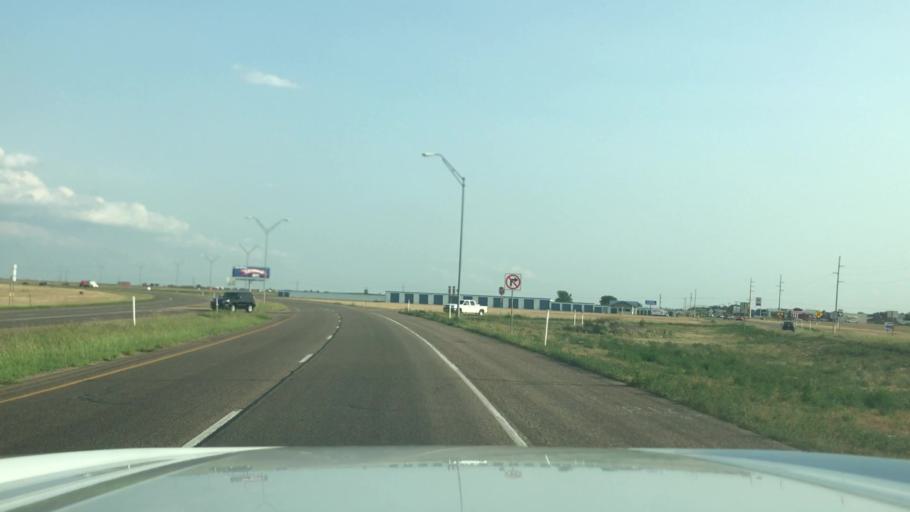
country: US
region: Texas
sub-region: Randall County
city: Canyon
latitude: 35.1216
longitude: -101.9377
